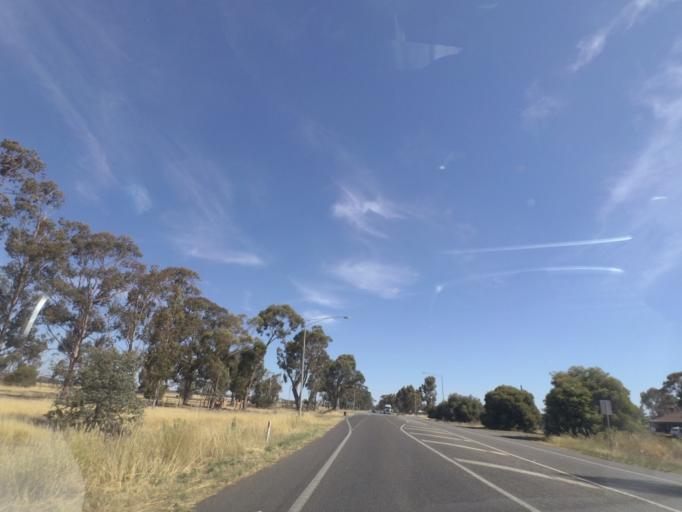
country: AU
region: Victoria
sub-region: Greater Shepparton
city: Shepparton
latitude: -36.4394
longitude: 145.3889
